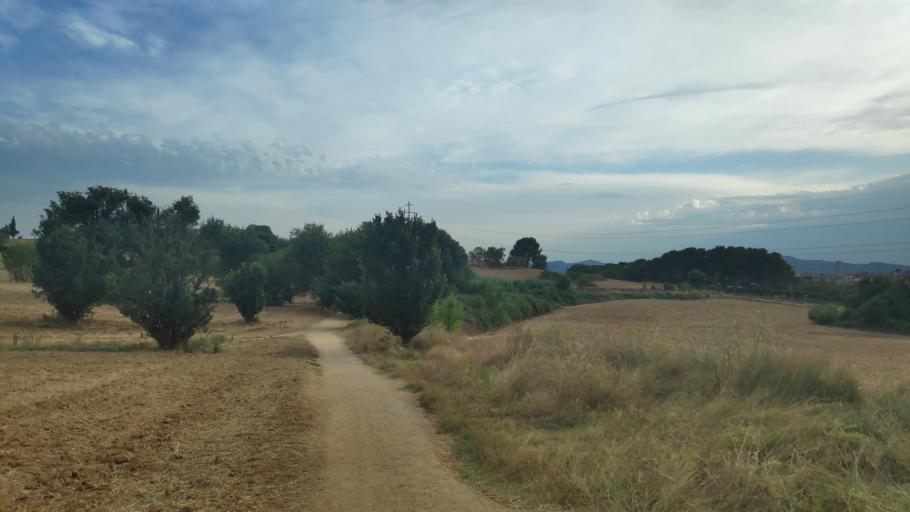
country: ES
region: Catalonia
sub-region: Provincia de Barcelona
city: Rubi
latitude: 41.4968
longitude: 2.0467
